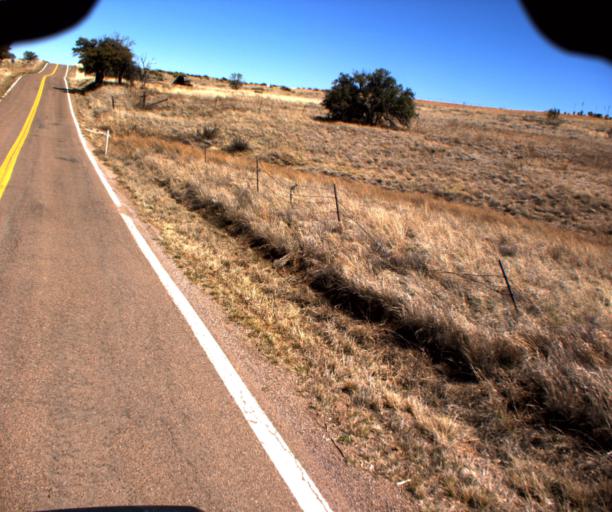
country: US
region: Arizona
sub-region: Cochise County
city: Huachuca City
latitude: 31.6008
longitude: -110.5782
